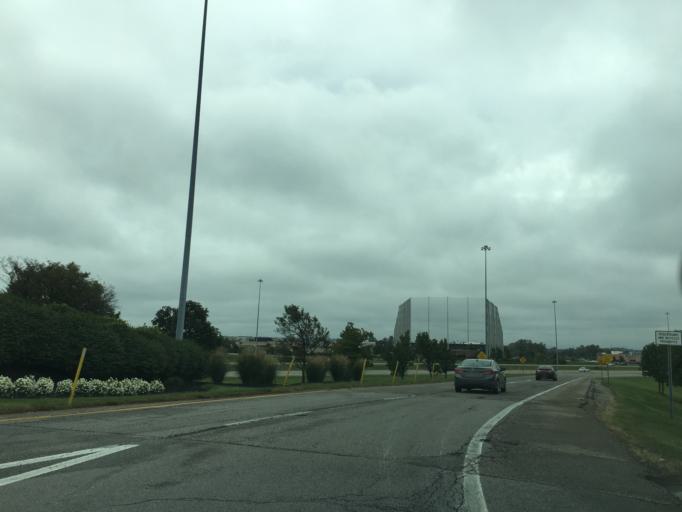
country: US
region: Ohio
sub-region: Butler County
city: Beckett Ridge
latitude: 39.3229
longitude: -84.4257
